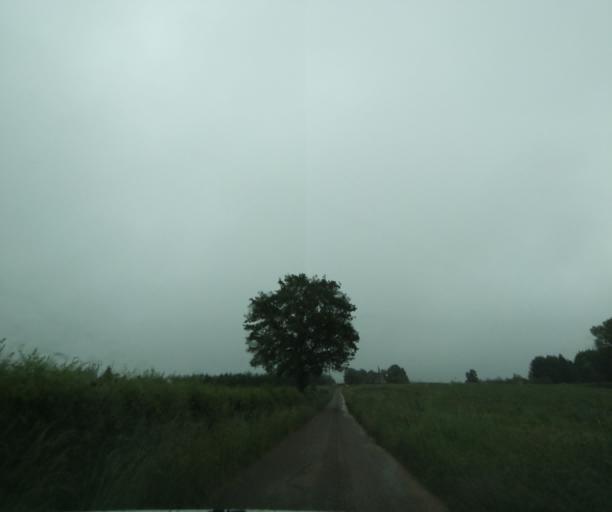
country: FR
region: Bourgogne
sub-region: Departement de Saone-et-Loire
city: Charolles
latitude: 46.3908
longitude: 4.3677
